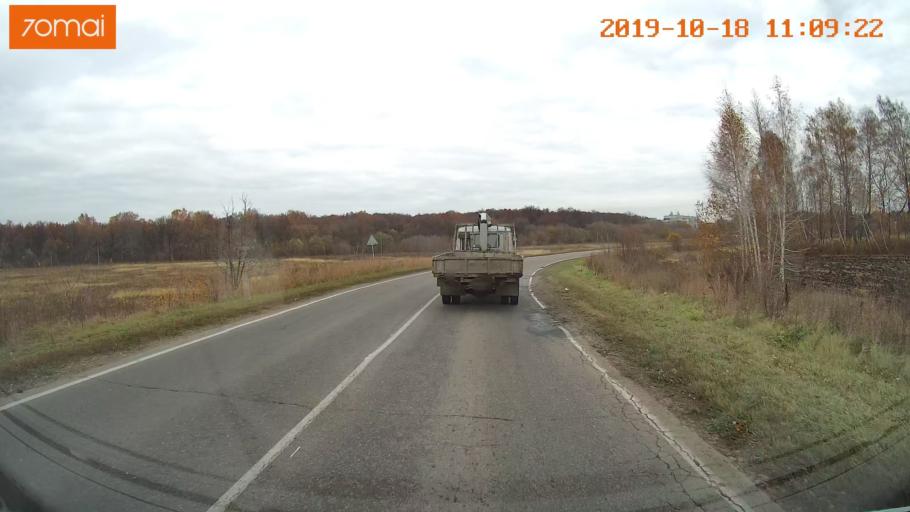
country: RU
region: Tula
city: Kimovsk
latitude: 53.9533
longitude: 38.5335
